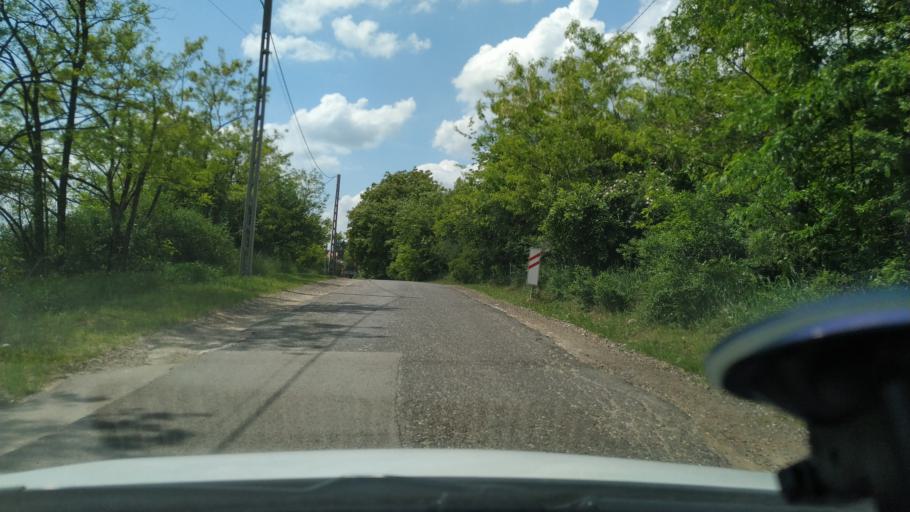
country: HU
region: Pest
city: Mende
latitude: 47.4395
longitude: 19.4719
